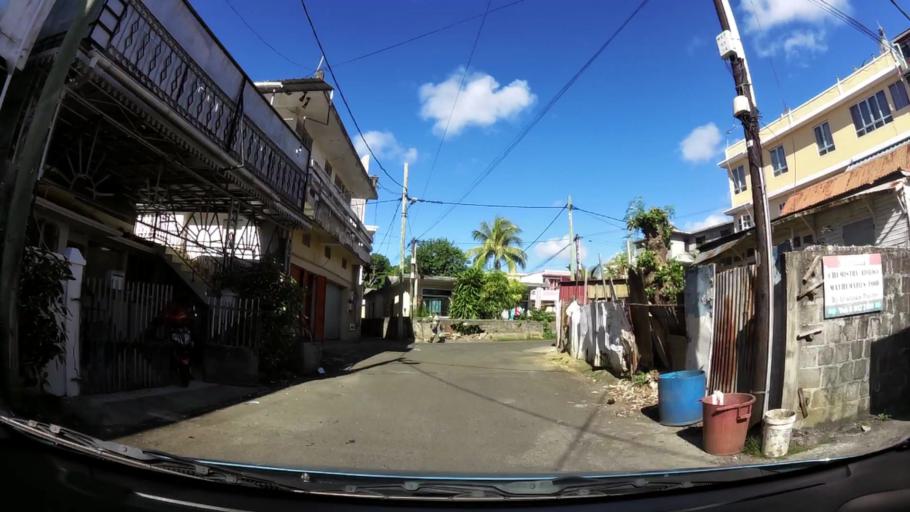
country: MU
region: Grand Port
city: Mahebourg
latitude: -20.4143
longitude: 57.7082
